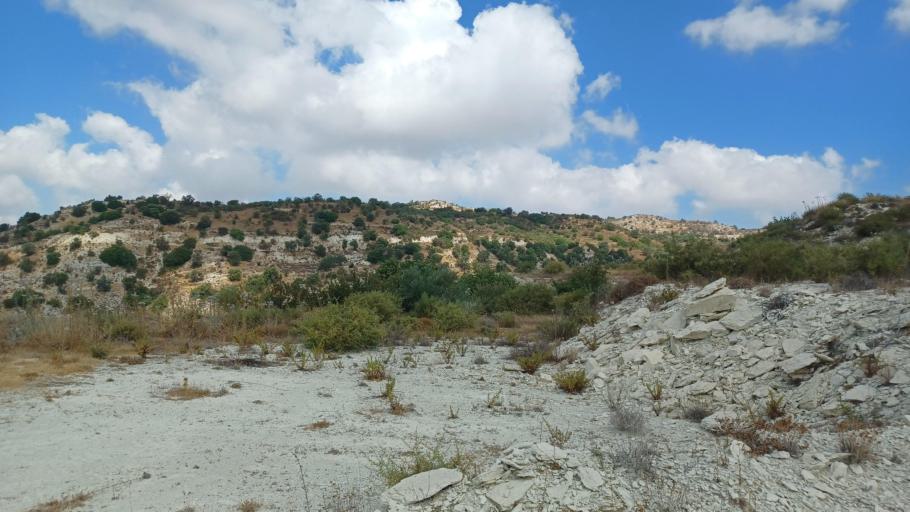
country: CY
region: Limassol
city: Pachna
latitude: 34.7990
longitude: 32.6643
